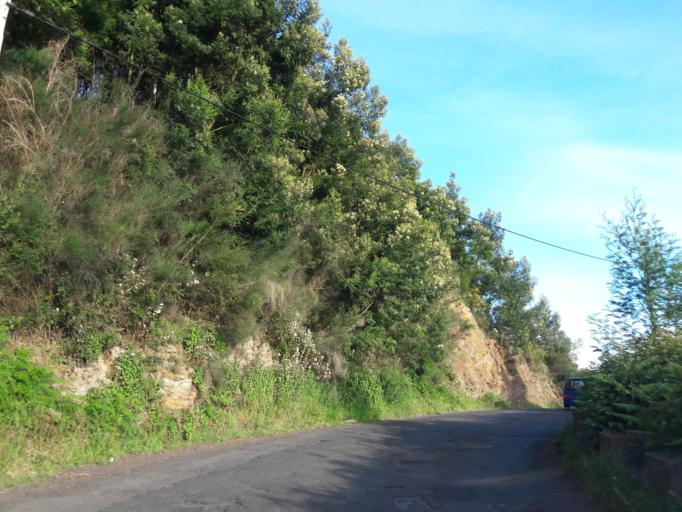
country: PT
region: Madeira
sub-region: Santa Cruz
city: Camacha
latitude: 32.6669
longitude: -16.8428
